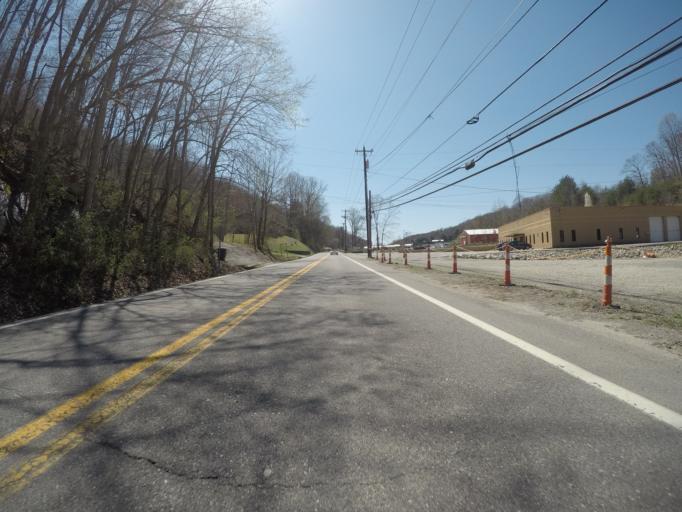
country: US
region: West Virginia
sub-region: Kanawha County
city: Charleston
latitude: 38.3787
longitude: -81.5640
